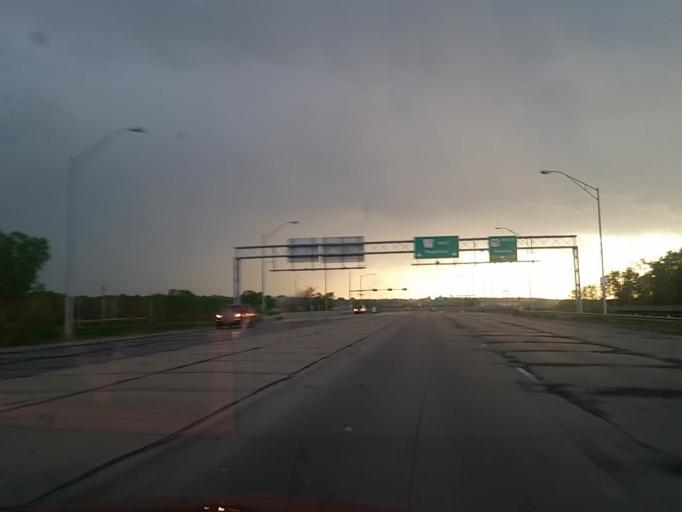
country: US
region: Nebraska
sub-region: Sarpy County
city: Offutt Air Force Base
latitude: 41.1402
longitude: -95.9315
